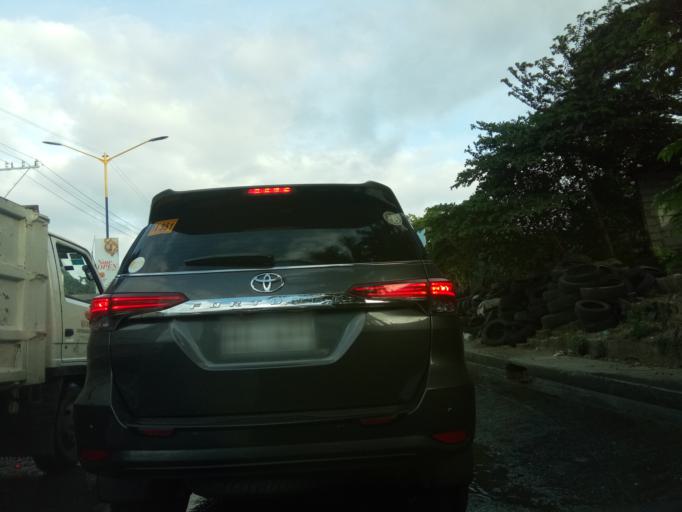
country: PH
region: Calabarzon
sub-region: Province of Cavite
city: Imus
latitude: 14.3865
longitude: 120.9757
